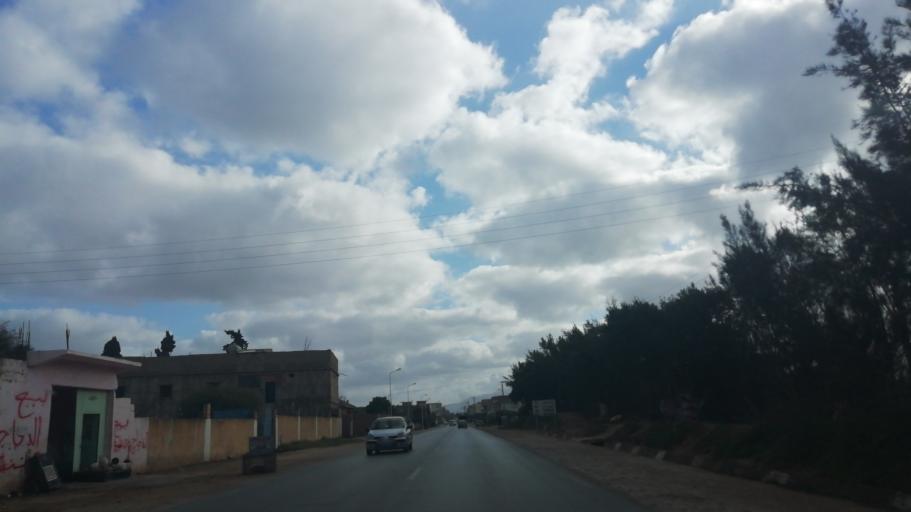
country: DZ
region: Relizane
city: Mazouna
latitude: 36.2590
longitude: 0.6013
